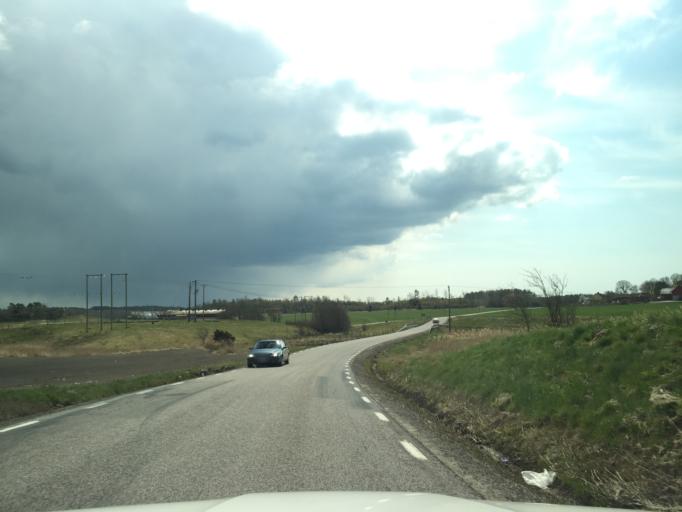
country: SE
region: Vaestra Goetaland
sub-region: Kungalvs Kommun
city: Kode
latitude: 57.9356
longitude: 11.8242
